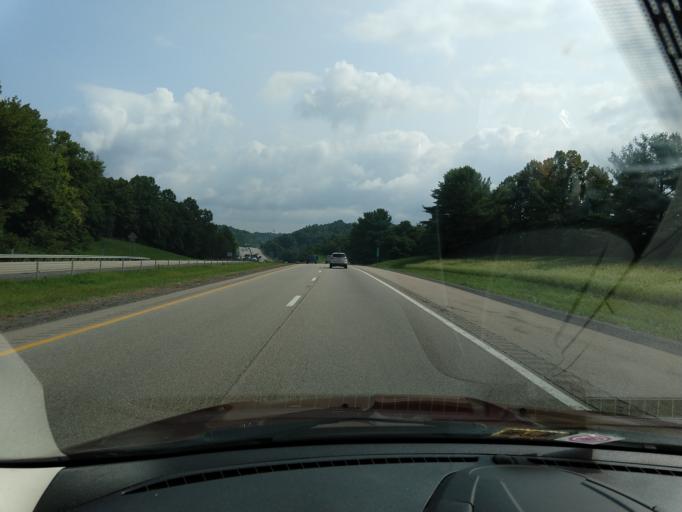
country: US
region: West Virginia
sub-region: Marion County
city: Pleasant Valley
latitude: 39.4523
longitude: -80.1502
